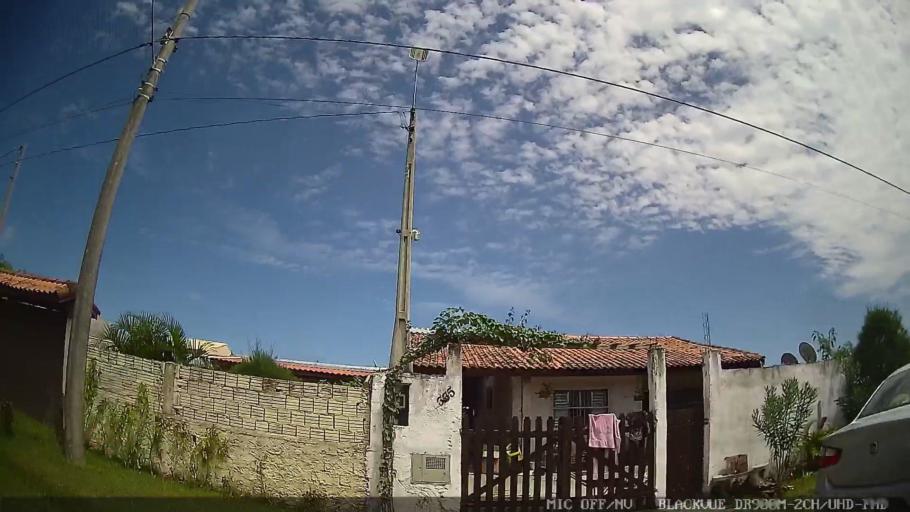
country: BR
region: Sao Paulo
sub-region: Iguape
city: Iguape
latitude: -24.7286
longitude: -47.5208
